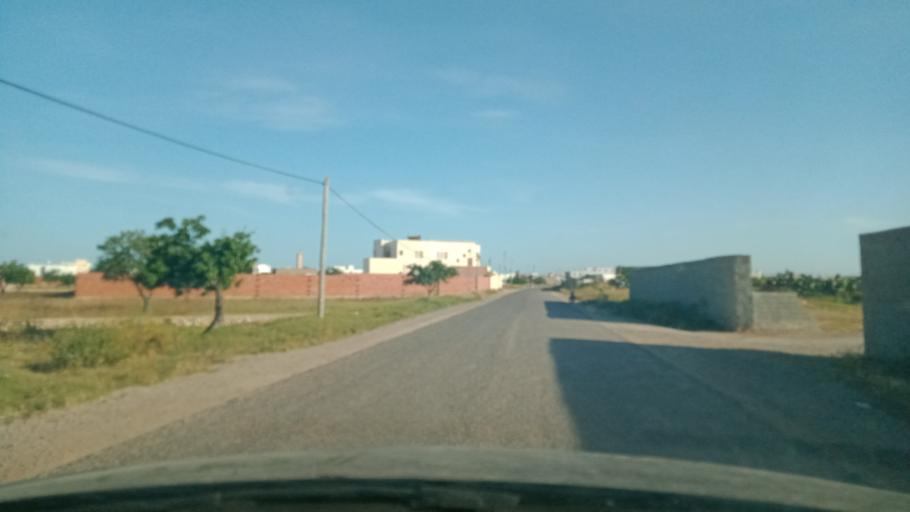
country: TN
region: Safaqis
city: Sfax
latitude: 34.8198
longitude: 10.7358
